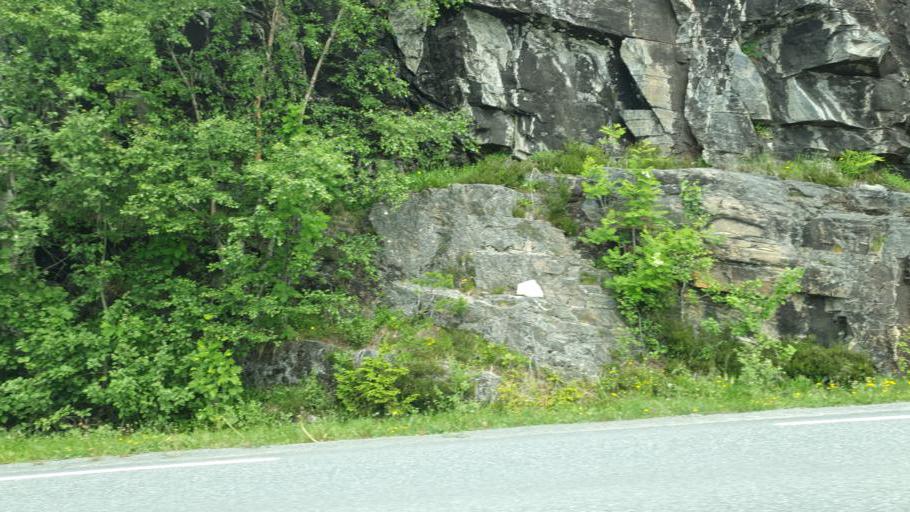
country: NO
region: Sor-Trondelag
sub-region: Trondheim
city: Trondheim
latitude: 63.5744
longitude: 10.3567
